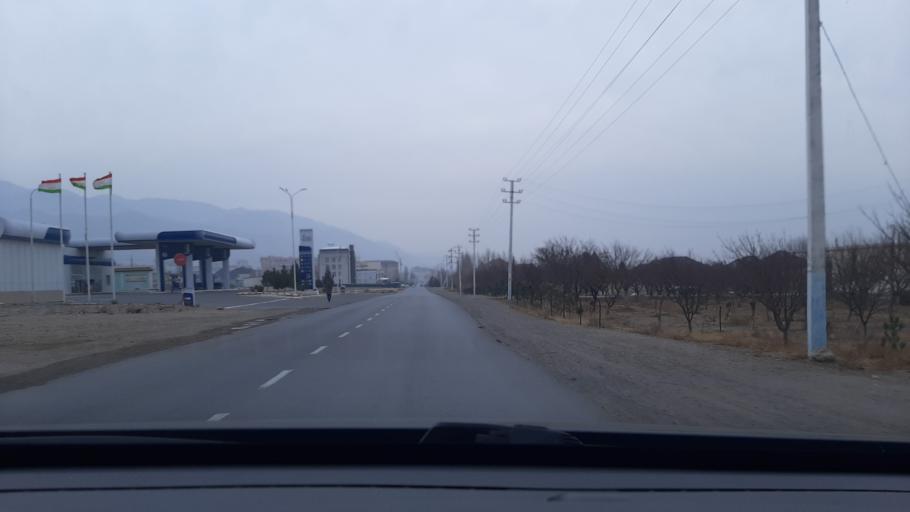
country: TJ
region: Viloyati Sughd
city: Khujand
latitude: 40.2764
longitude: 69.5804
